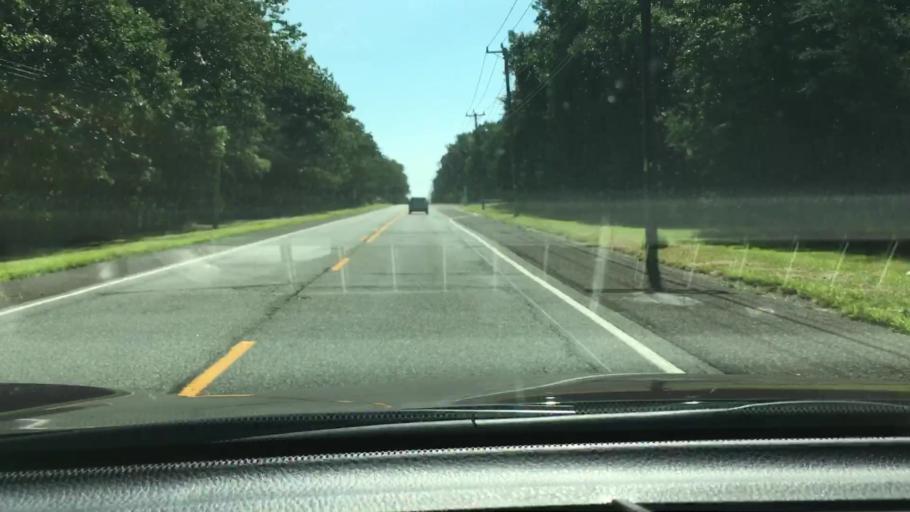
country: US
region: New Jersey
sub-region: Cumberland County
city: Millville
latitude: 39.3822
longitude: -74.9748
